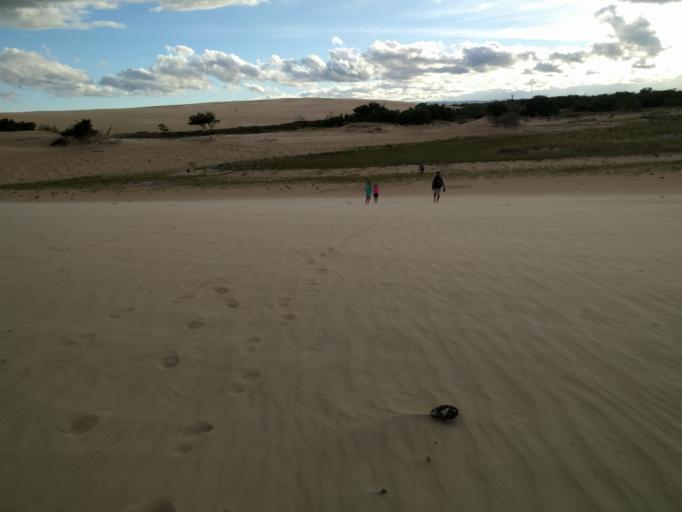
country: BO
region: Santa Cruz
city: Cotoca
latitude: -17.9750
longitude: -63.1447
